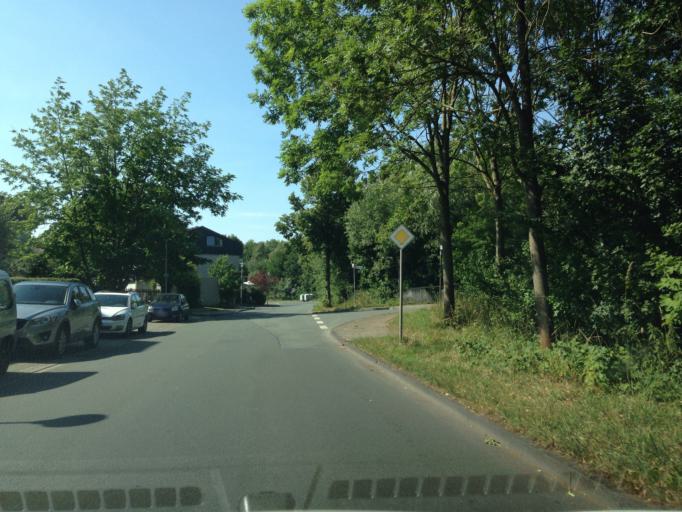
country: DE
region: North Rhine-Westphalia
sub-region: Regierungsbezirk Munster
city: Muenster
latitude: 51.9698
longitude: 7.5723
